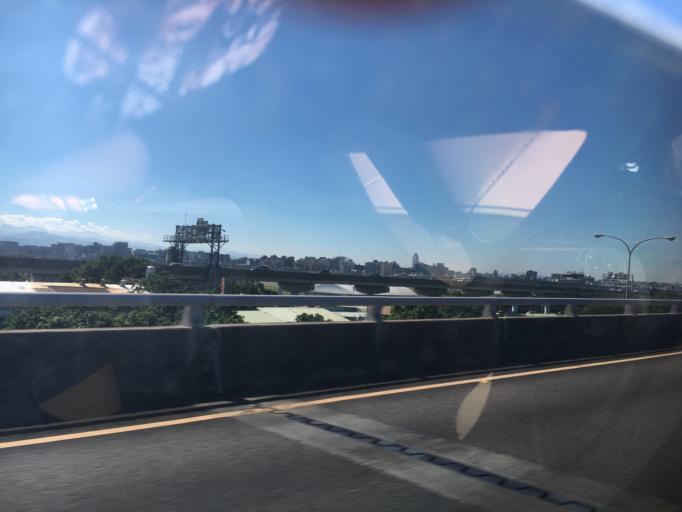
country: TW
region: Taipei
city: Taipei
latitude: 25.0732
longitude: 121.5557
